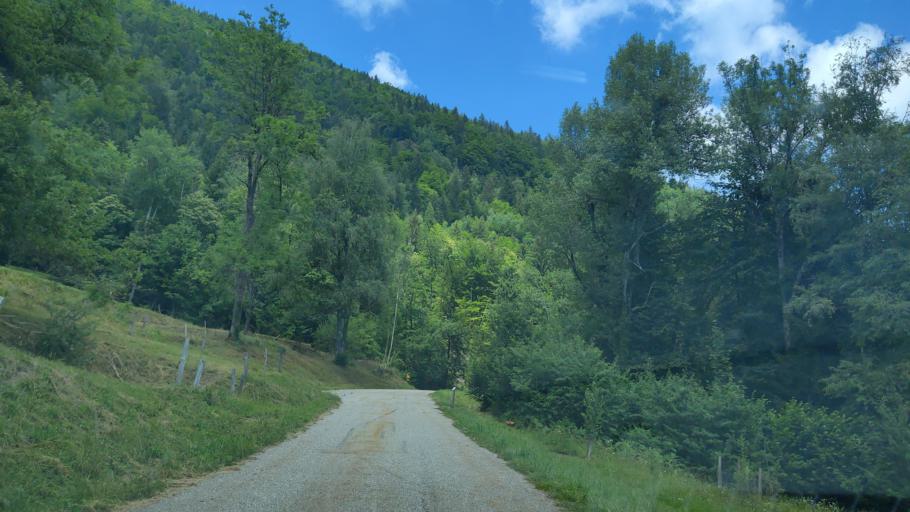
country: FR
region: Rhone-Alpes
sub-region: Departement de la Savoie
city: Aiton
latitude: 45.5112
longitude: 6.2802
